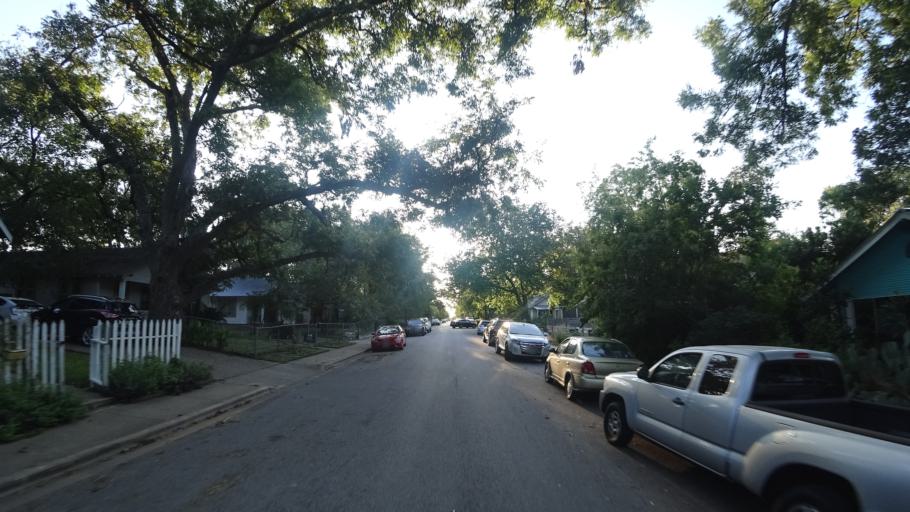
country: US
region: Texas
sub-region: Travis County
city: Austin
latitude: 30.2554
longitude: -97.7290
